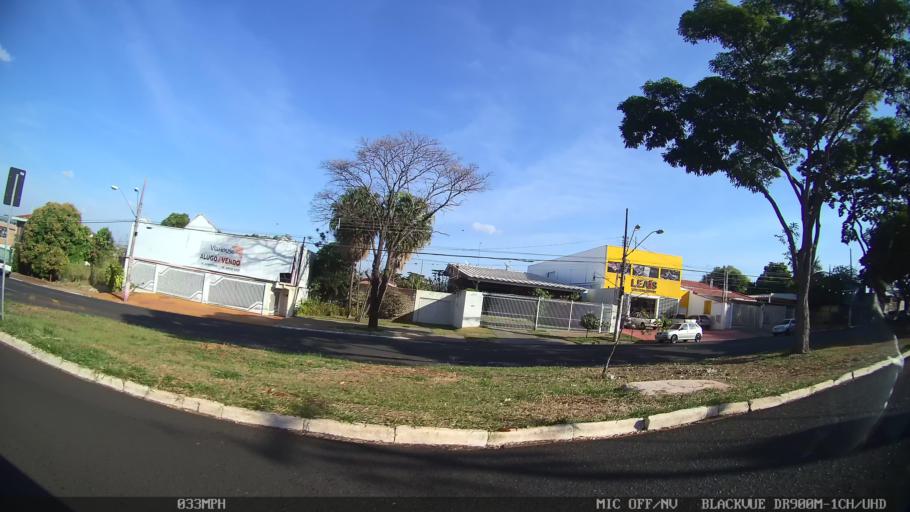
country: BR
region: Sao Paulo
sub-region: Ribeirao Preto
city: Ribeirao Preto
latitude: -21.2040
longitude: -47.7765
